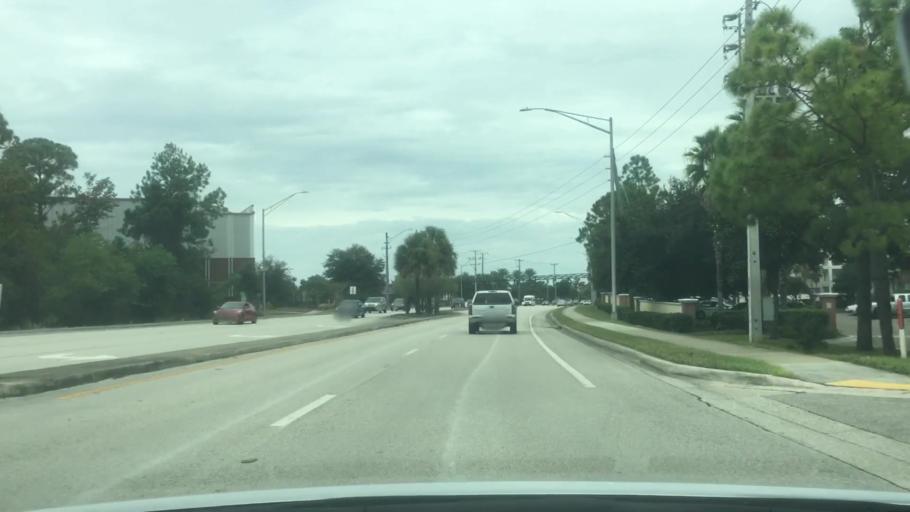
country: US
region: Florida
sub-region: Duval County
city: Jacksonville
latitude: 30.3362
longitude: -81.5460
